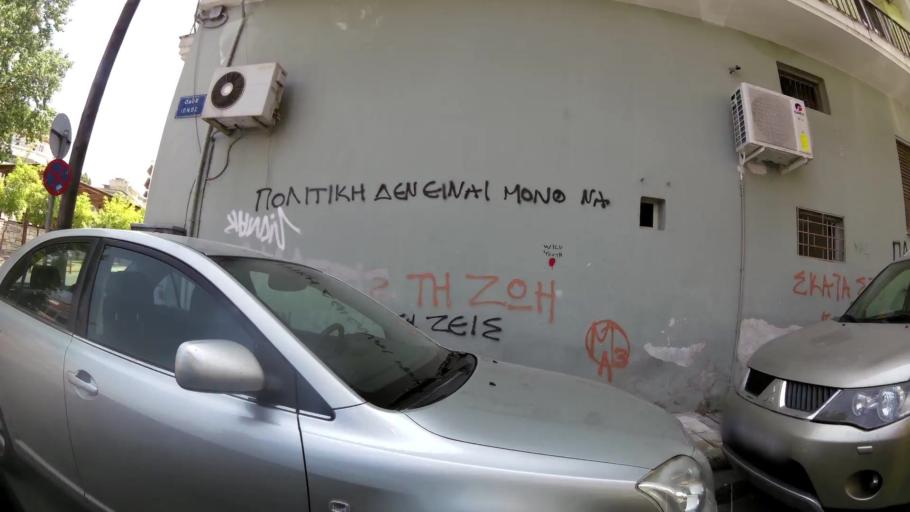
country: GR
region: Central Macedonia
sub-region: Nomos Imathias
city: Veroia
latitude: 40.5201
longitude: 22.1994
